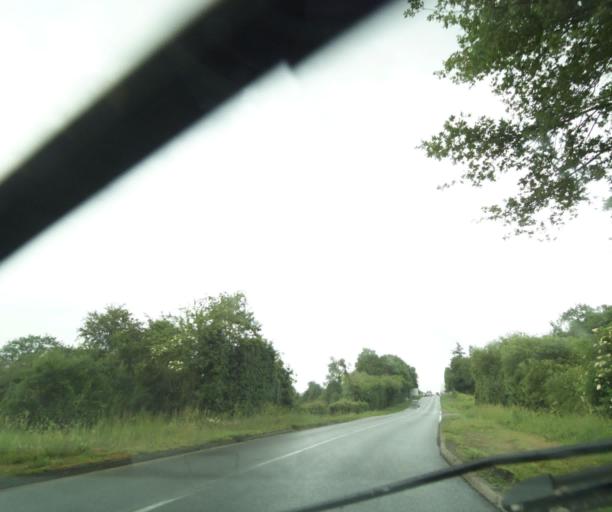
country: FR
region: Poitou-Charentes
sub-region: Departement des Deux-Sevres
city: Chatillon-sur-Thouet
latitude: 46.6651
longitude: -0.2477
